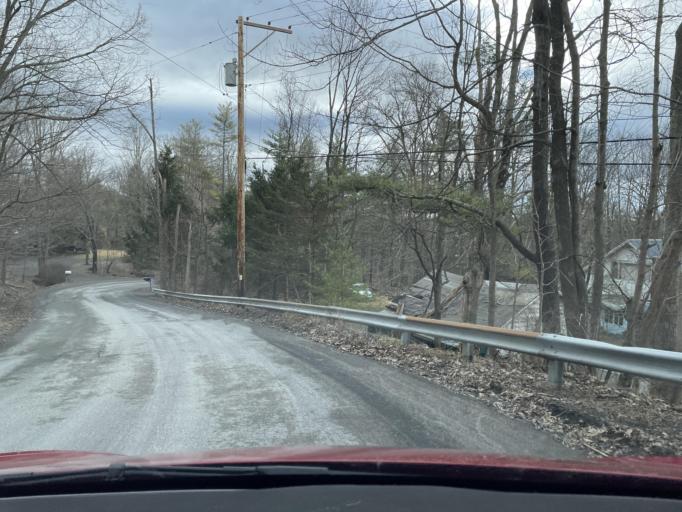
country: US
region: New York
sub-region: Ulster County
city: Woodstock
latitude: 42.0551
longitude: -74.1194
